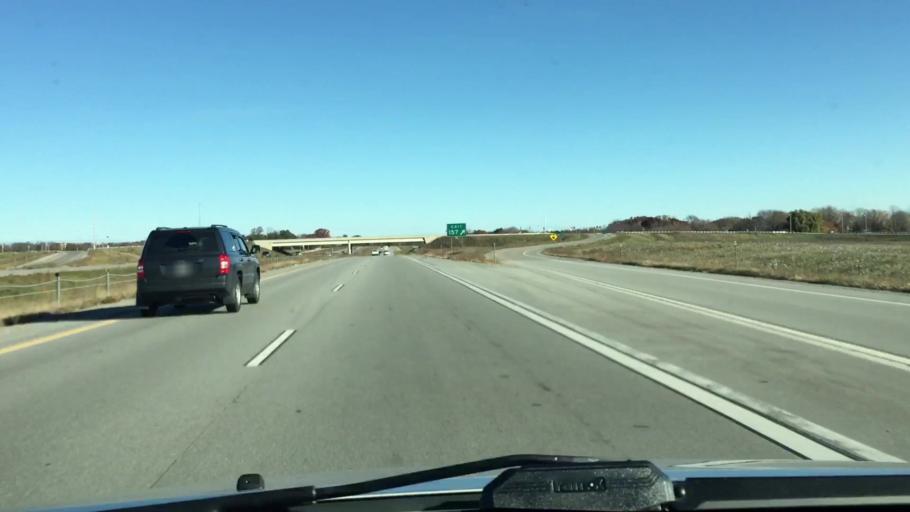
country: US
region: Wisconsin
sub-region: Brown County
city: Wrightstown
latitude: 44.3830
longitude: -88.1639
